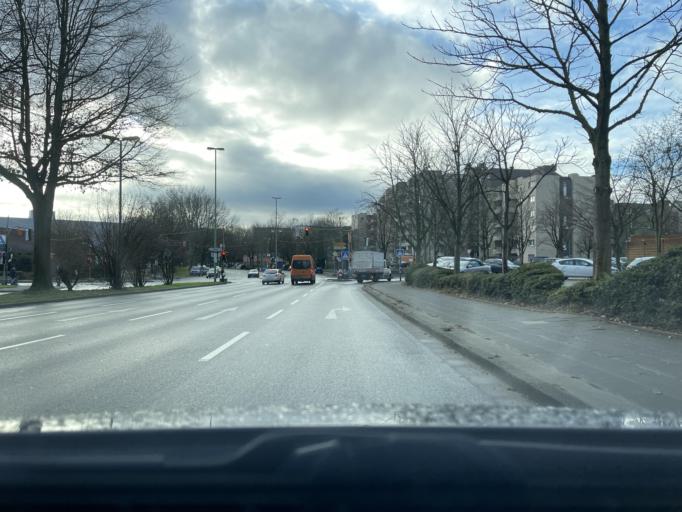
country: DE
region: North Rhine-Westphalia
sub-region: Regierungsbezirk Munster
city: Bottrop
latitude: 51.4732
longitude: 6.9561
